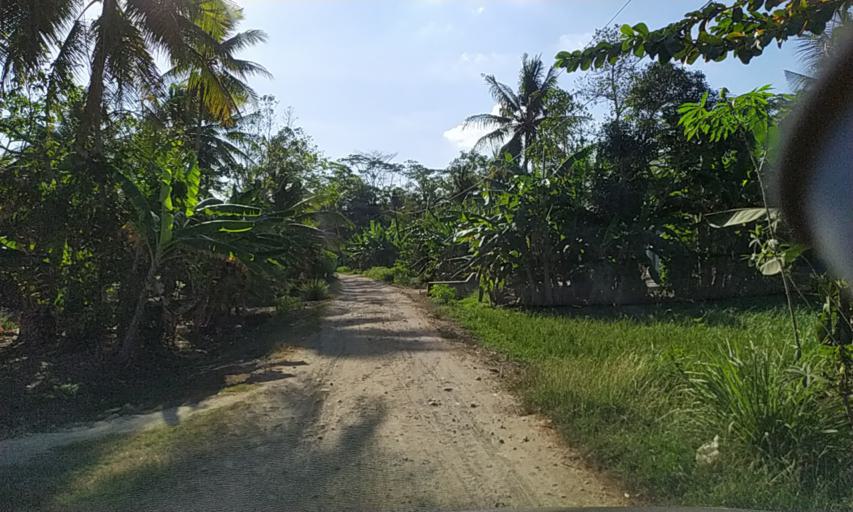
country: ID
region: Central Java
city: Kalenaren
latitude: -7.5937
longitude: 108.8053
